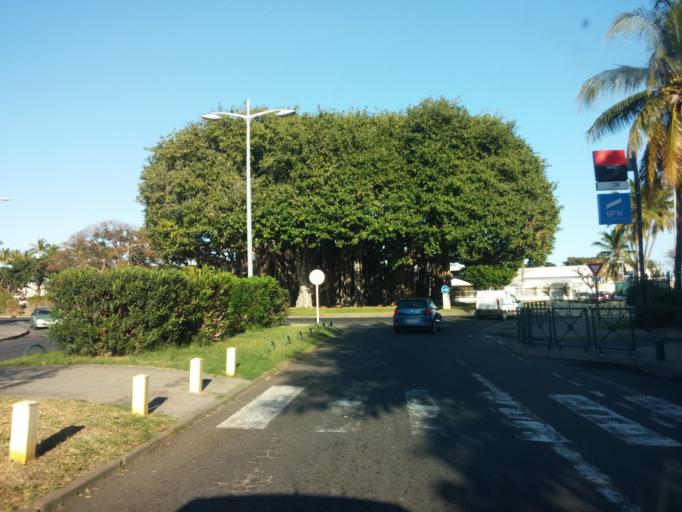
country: RE
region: Reunion
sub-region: Reunion
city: Le Port
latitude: -20.9333
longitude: 55.2925
